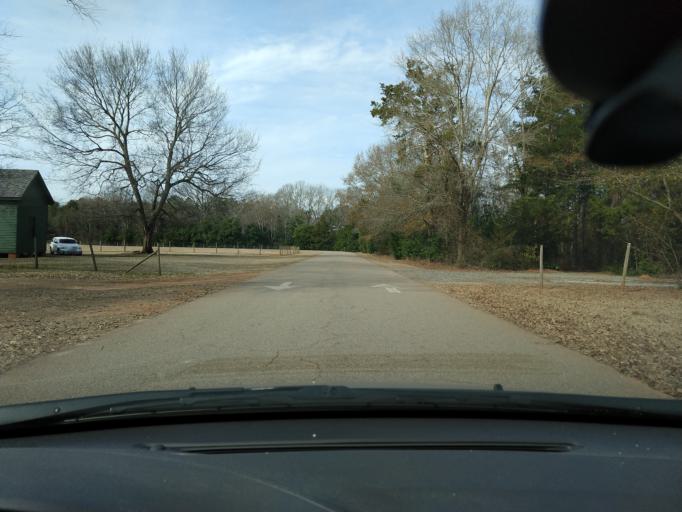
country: US
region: Georgia
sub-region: Webster County
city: Preston
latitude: 32.0257
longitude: -84.4302
